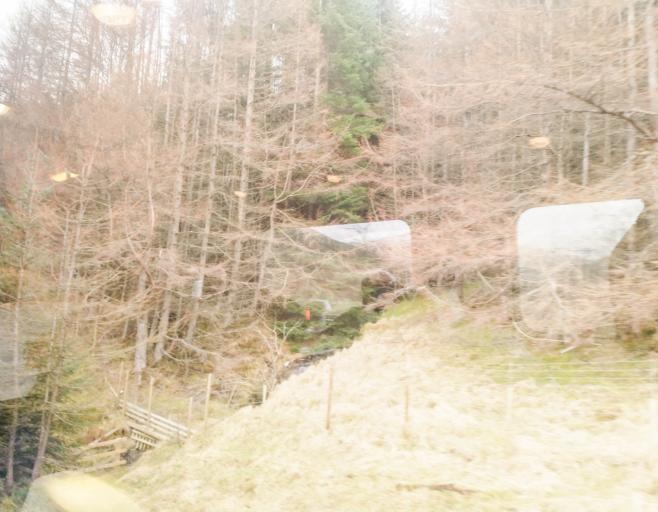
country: GB
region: Scotland
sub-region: Argyll and Bute
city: Garelochhead
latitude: 56.4390
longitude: -4.7068
